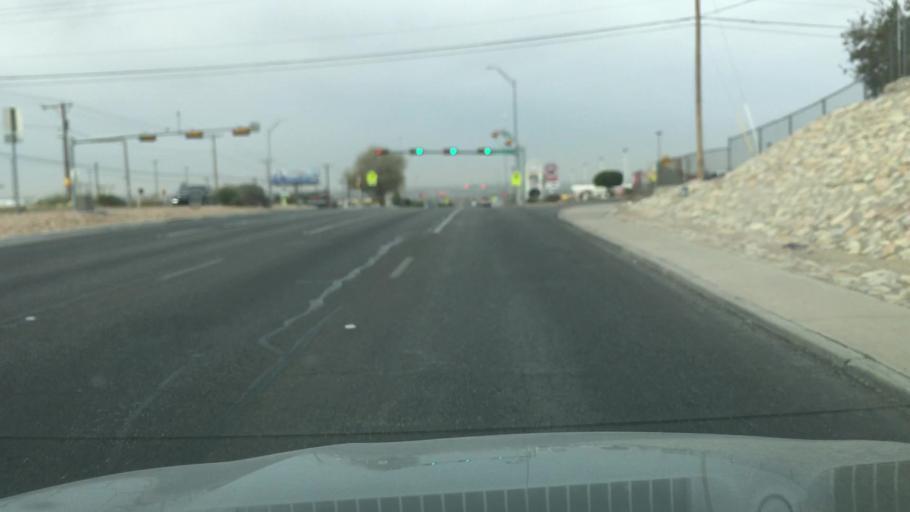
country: US
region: New Mexico
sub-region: Dona Ana County
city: Sunland Park
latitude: 31.8350
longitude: -106.5462
